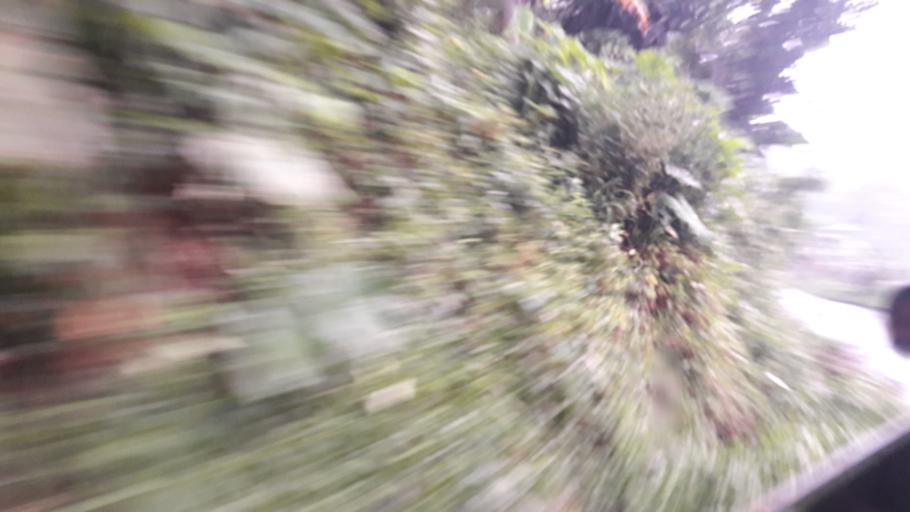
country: ID
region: West Java
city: Cipeundeuy
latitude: -6.6480
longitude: 106.5204
